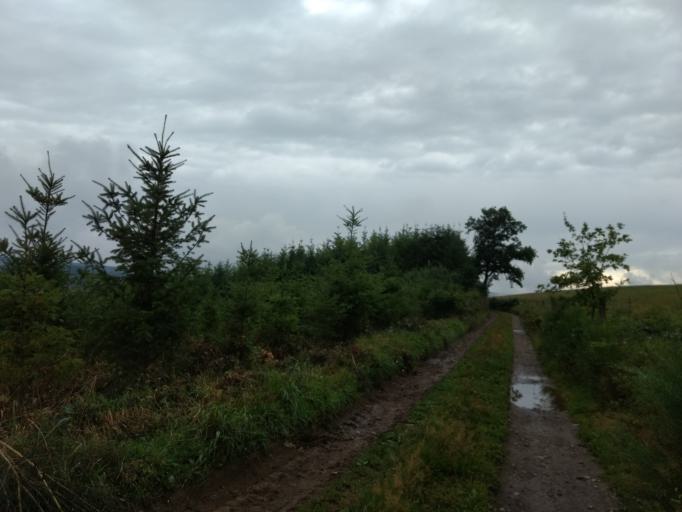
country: BE
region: Wallonia
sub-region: Province du Luxembourg
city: Bertogne
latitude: 50.1430
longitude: 5.7097
